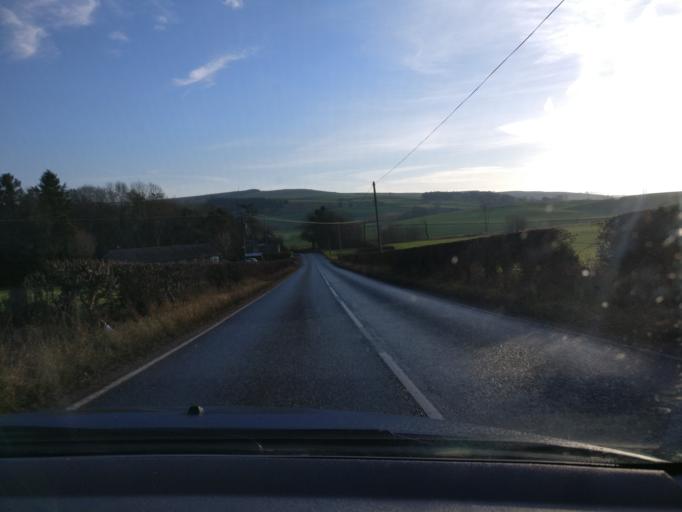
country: GB
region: Scotland
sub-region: The Scottish Borders
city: Jedburgh
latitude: 55.4692
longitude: -2.6538
